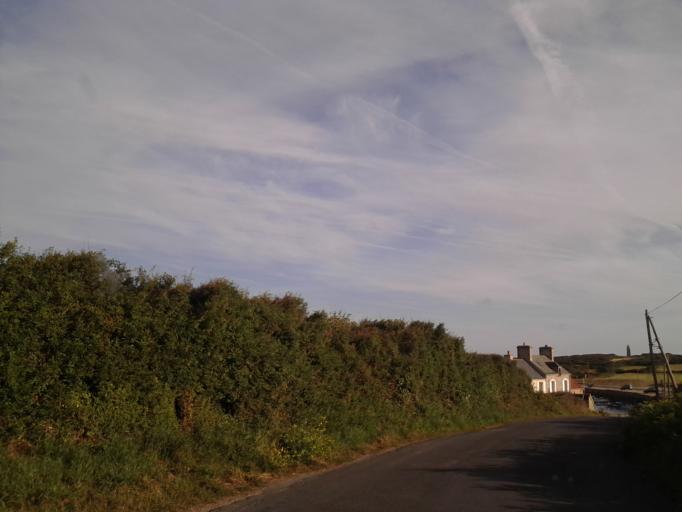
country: FR
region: Lower Normandy
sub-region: Departement de la Manche
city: Fermanville
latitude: 49.6853
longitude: -1.4724
